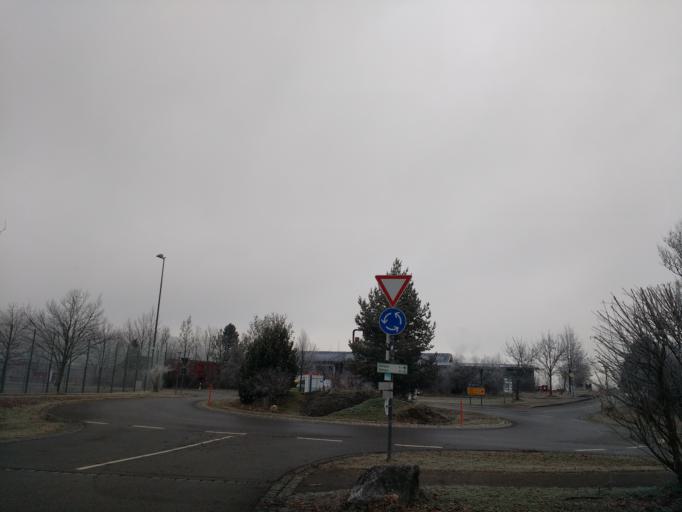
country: DE
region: Bavaria
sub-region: Swabia
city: Wildpoldsried
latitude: 47.7685
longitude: 10.3992
